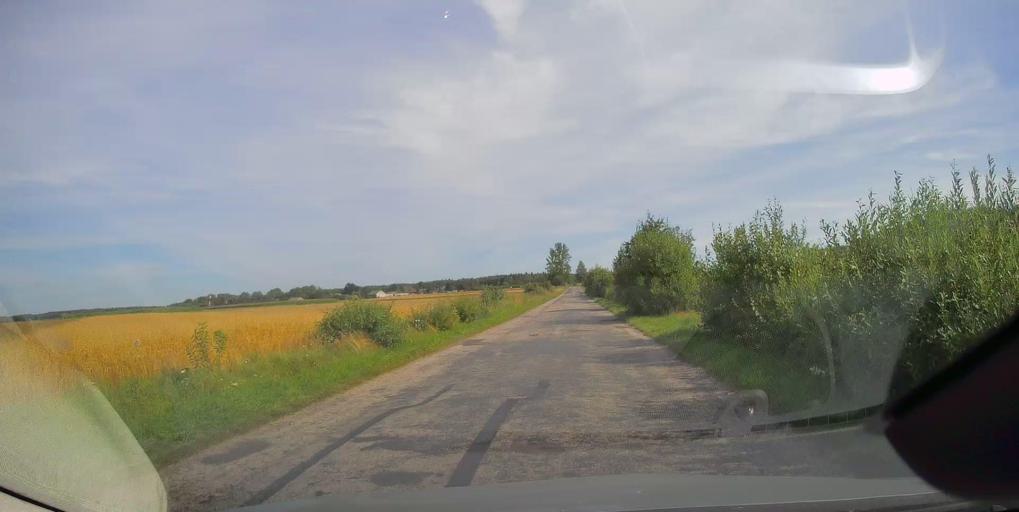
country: PL
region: Lodz Voivodeship
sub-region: Powiat opoczynski
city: Mniszkow
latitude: 51.4148
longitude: 20.0332
